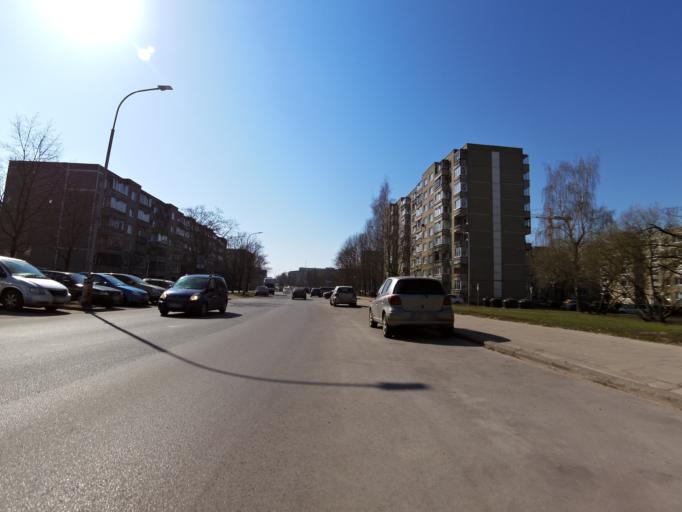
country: LT
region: Vilnius County
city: Justiniskes
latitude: 54.7203
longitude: 25.2141
